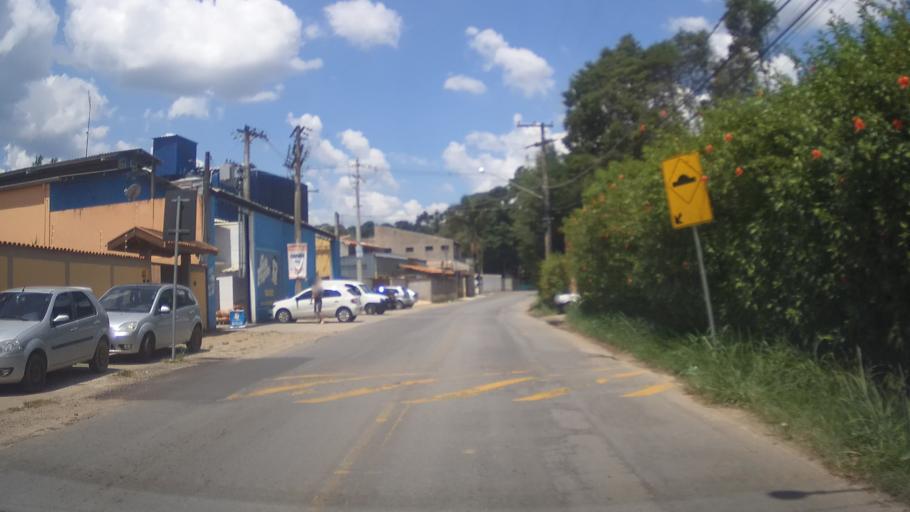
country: BR
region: Sao Paulo
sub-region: Varzea Paulista
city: Varzea Paulista
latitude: -23.1485
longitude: -46.8307
